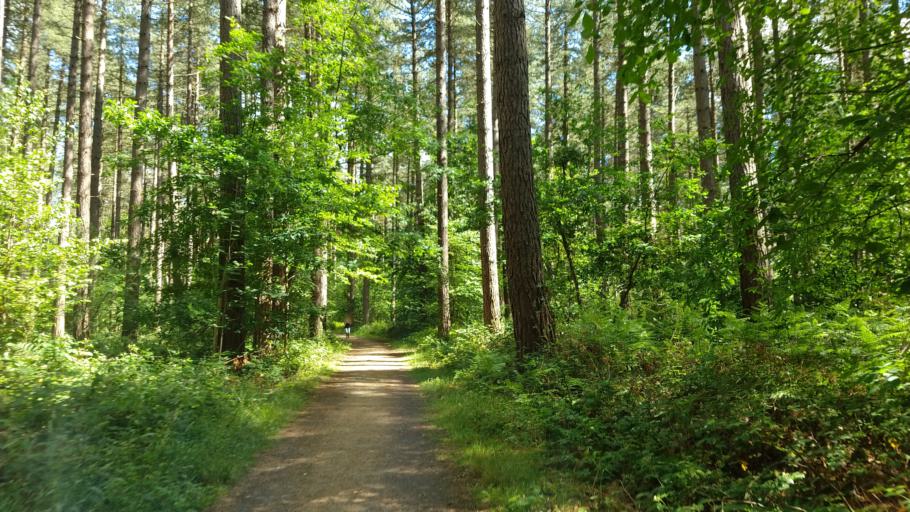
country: BE
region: Flanders
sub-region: Provincie Vlaams-Brabant
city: Bierbeek
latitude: 50.8176
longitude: 4.7266
